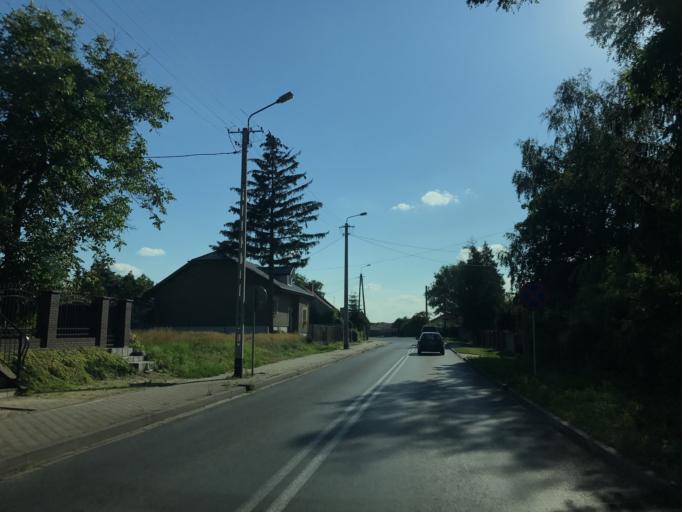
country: PL
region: Kujawsko-Pomorskie
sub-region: Powiat wloclawski
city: Brzesc Kujawski
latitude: 52.6013
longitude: 18.9006
